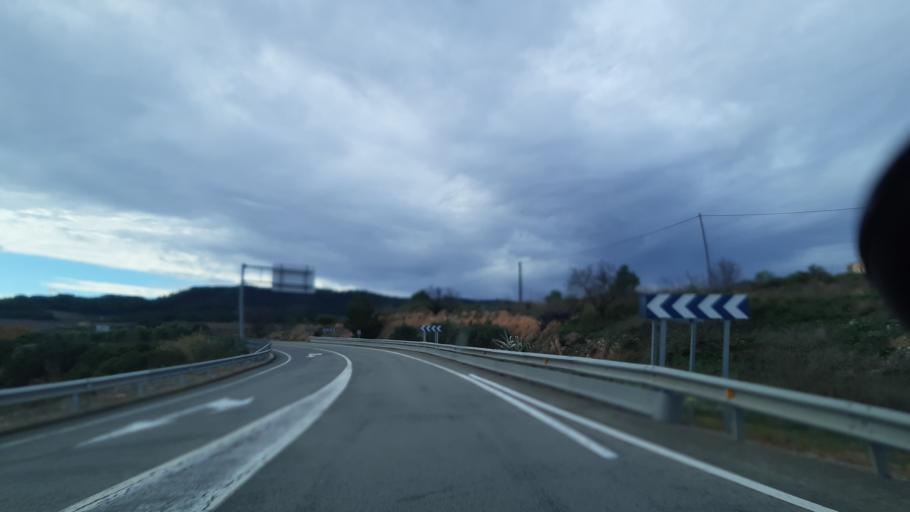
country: ES
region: Catalonia
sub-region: Provincia de Tarragona
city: la Fatarella
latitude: 41.1104
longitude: 0.5337
